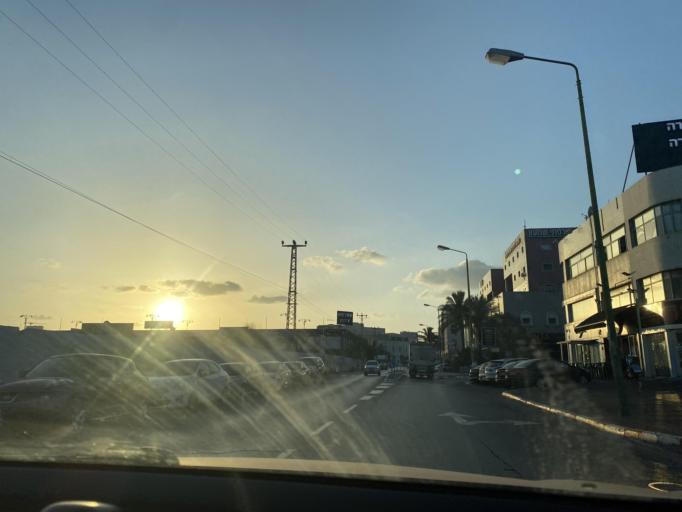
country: IL
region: Southern District
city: Ashdod
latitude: 31.8120
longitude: 34.6591
